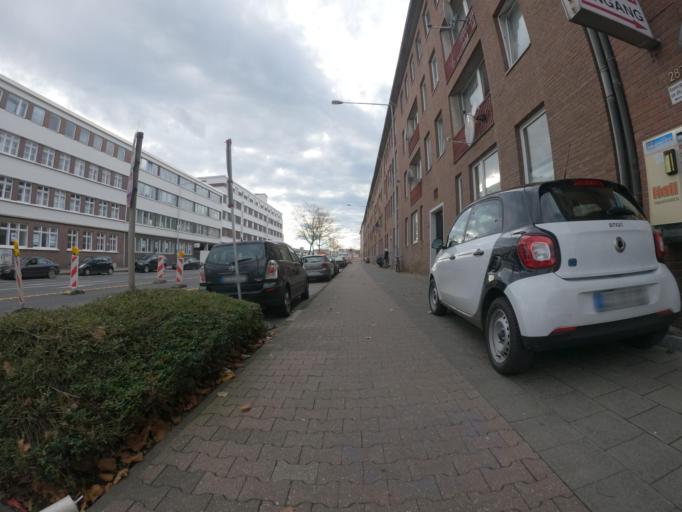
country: DE
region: North Rhine-Westphalia
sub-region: Regierungsbezirk Koln
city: Aachen
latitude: 50.7873
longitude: 6.1131
